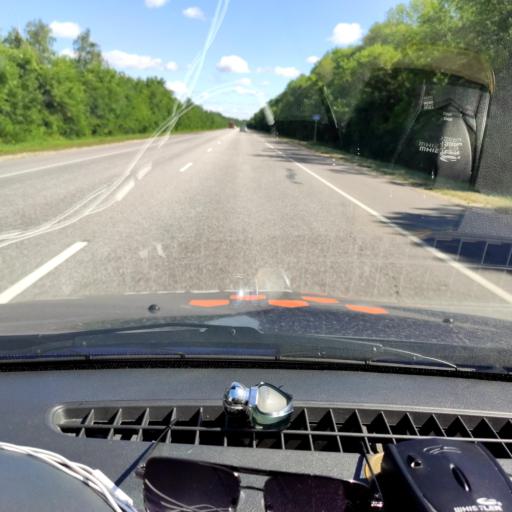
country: RU
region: Lipetsk
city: Borinskoye
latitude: 52.3607
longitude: 39.2007
